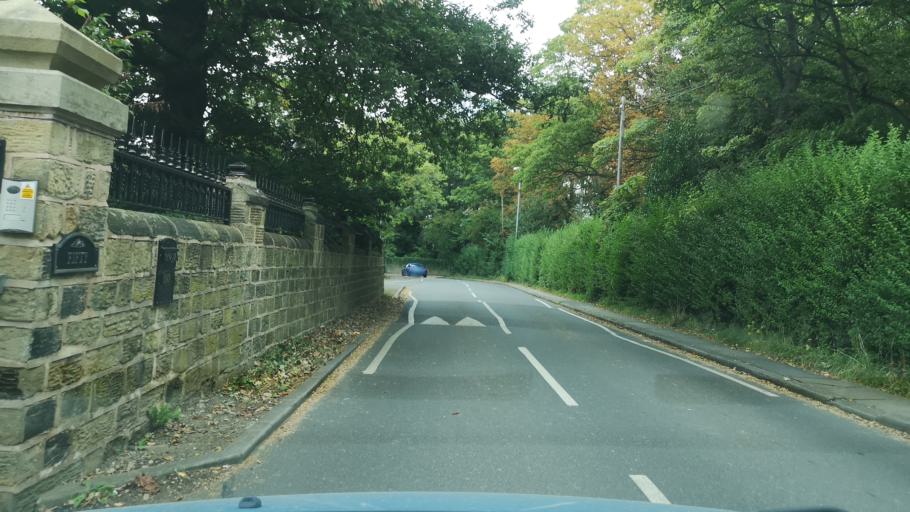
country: GB
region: England
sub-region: City and Borough of Wakefield
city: Walton
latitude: 53.6463
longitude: -1.4834
